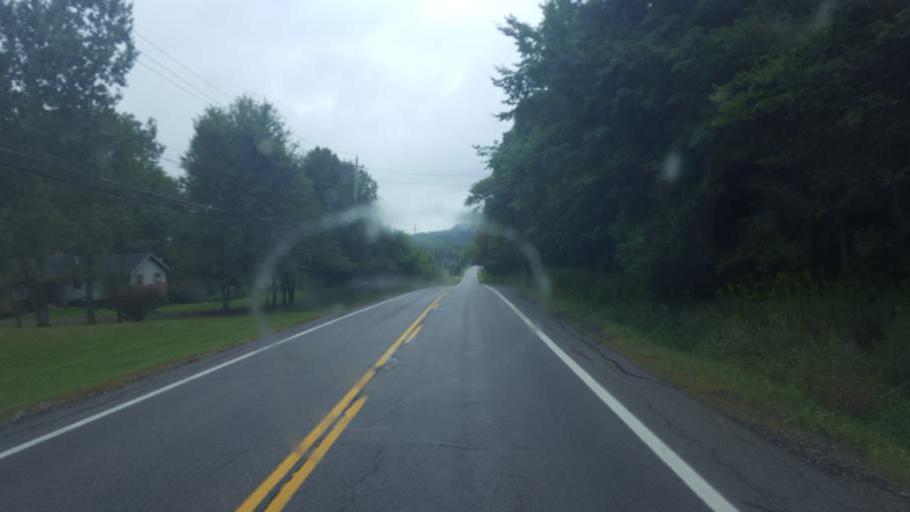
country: US
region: Ohio
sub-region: Geauga County
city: Burton
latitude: 41.5255
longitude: -81.1937
